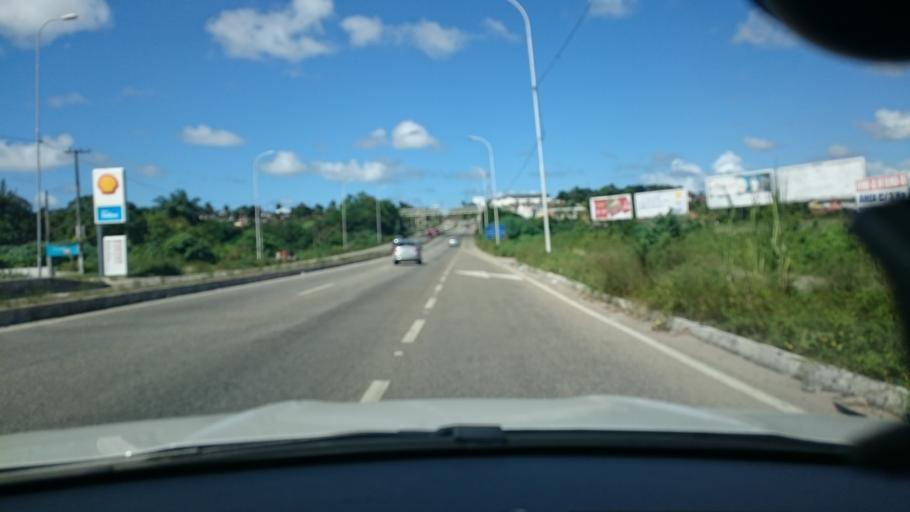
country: BR
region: Paraiba
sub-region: Joao Pessoa
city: Joao Pessoa
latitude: -7.1664
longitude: -34.8882
